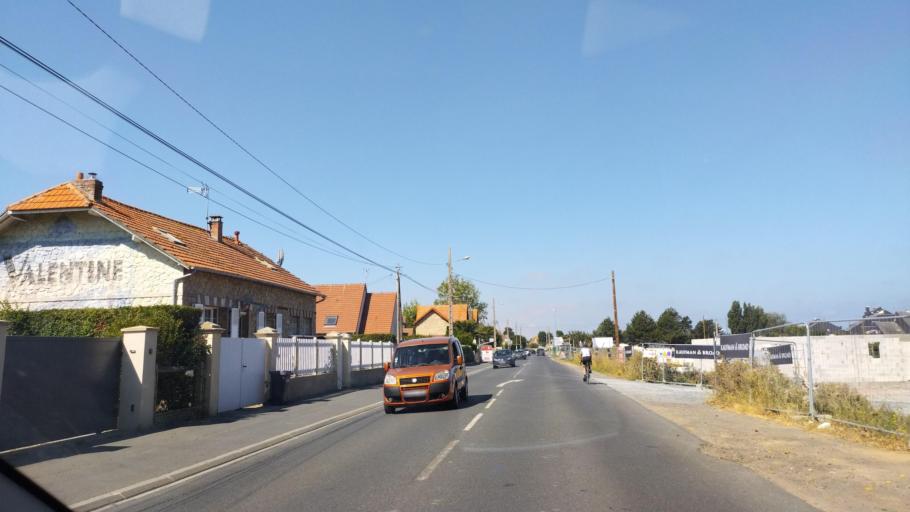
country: FR
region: Lower Normandy
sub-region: Departement du Calvados
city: Courseulles-sur-Mer
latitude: 49.3301
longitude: -0.4446
